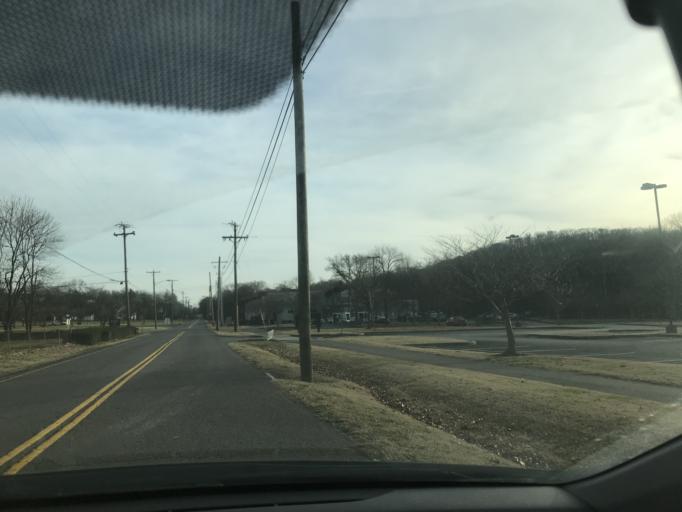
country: US
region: Tennessee
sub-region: Davidson County
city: Nashville
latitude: 36.2108
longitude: -86.8240
